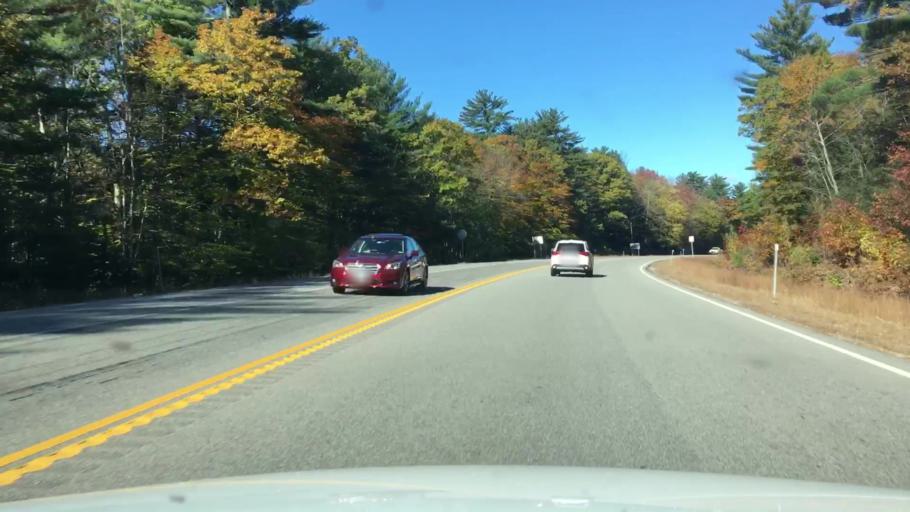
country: US
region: New Hampshire
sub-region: Carroll County
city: Sanbornville
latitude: 43.4990
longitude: -71.0275
